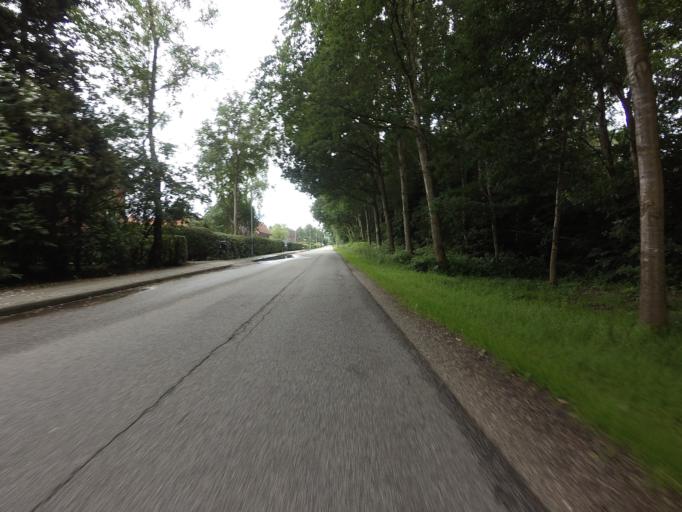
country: DK
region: Central Jutland
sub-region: Randers Kommune
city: Langa
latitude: 56.3891
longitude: 9.9010
